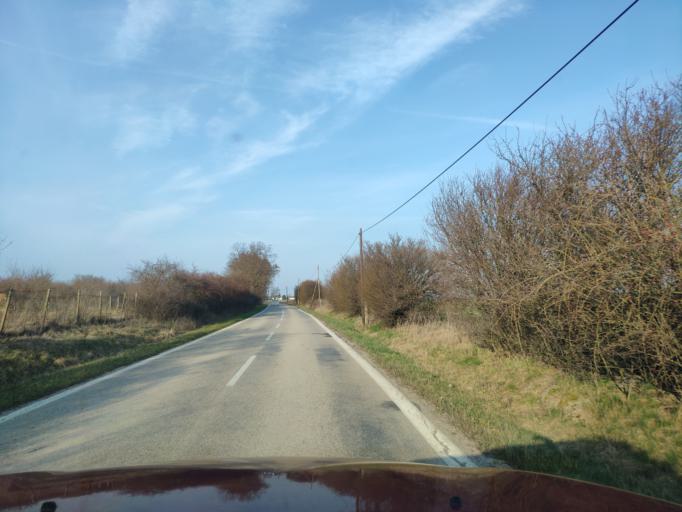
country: SK
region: Bratislavsky
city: Modra
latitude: 48.3139
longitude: 17.3648
